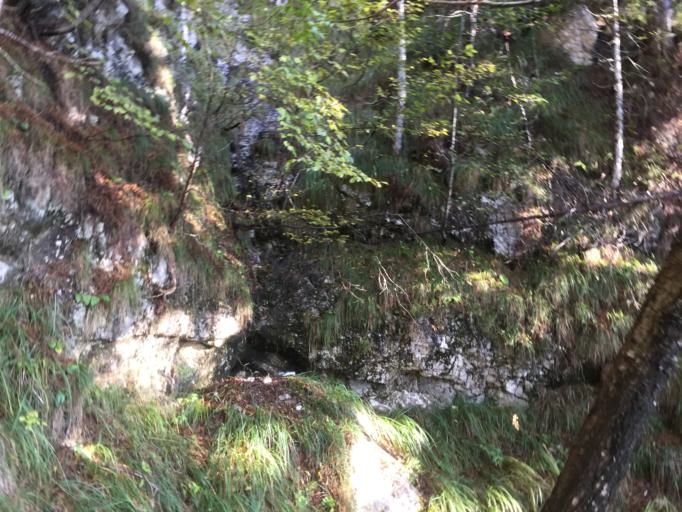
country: IT
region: Friuli Venezia Giulia
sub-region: Provincia di Udine
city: Chiusaforte
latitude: 46.4050
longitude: 13.3338
